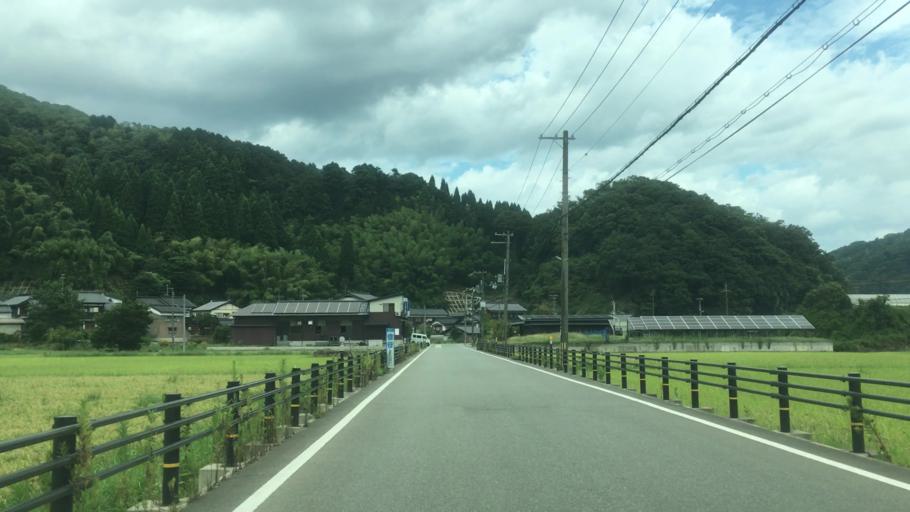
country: JP
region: Hyogo
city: Toyooka
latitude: 35.5920
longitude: 134.7984
